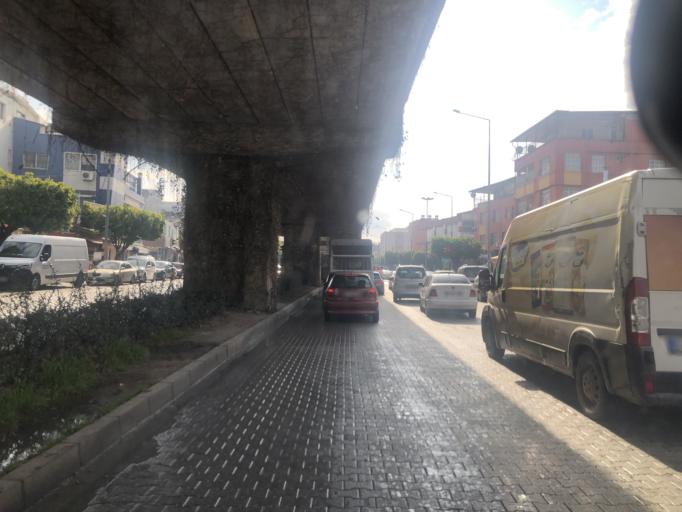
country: TR
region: Adana
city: Seyhan
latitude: 36.9831
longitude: 35.3203
